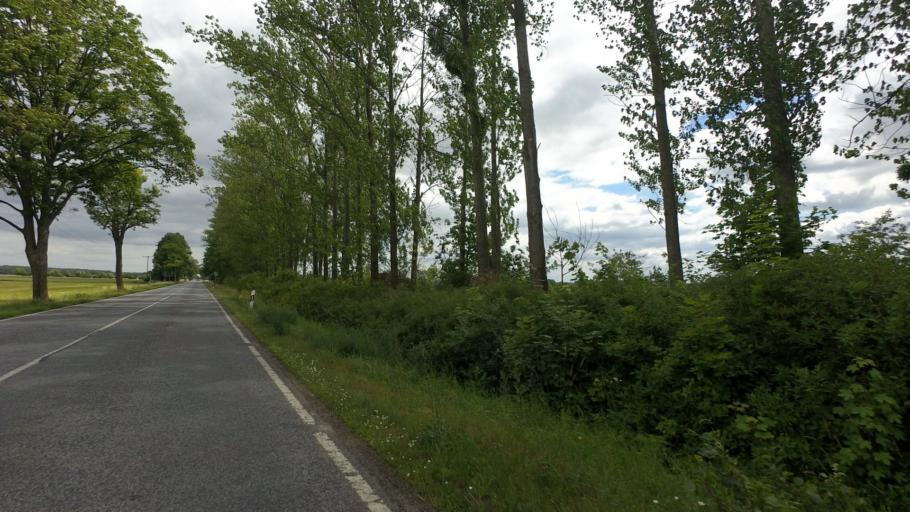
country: DE
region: Brandenburg
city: Luckau
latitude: 51.8408
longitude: 13.7513
